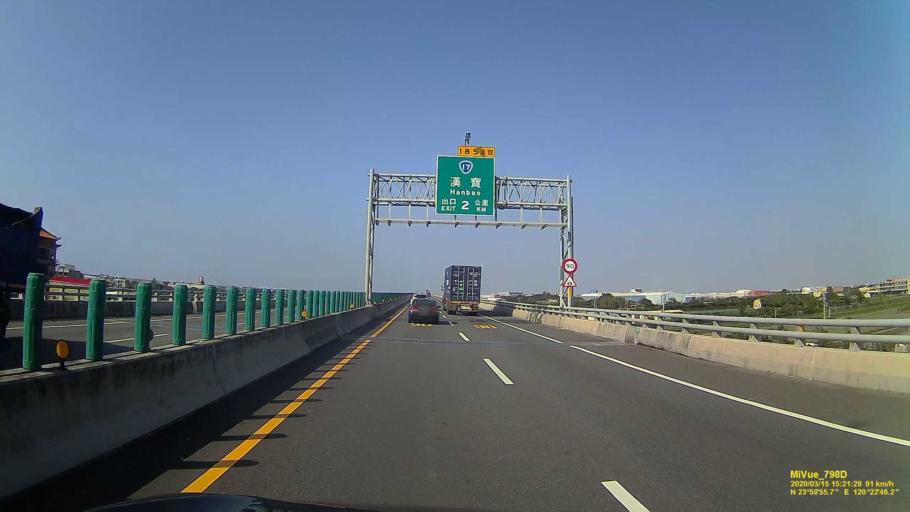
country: TW
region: Taiwan
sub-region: Changhua
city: Chang-hua
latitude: 23.9992
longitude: 120.3796
